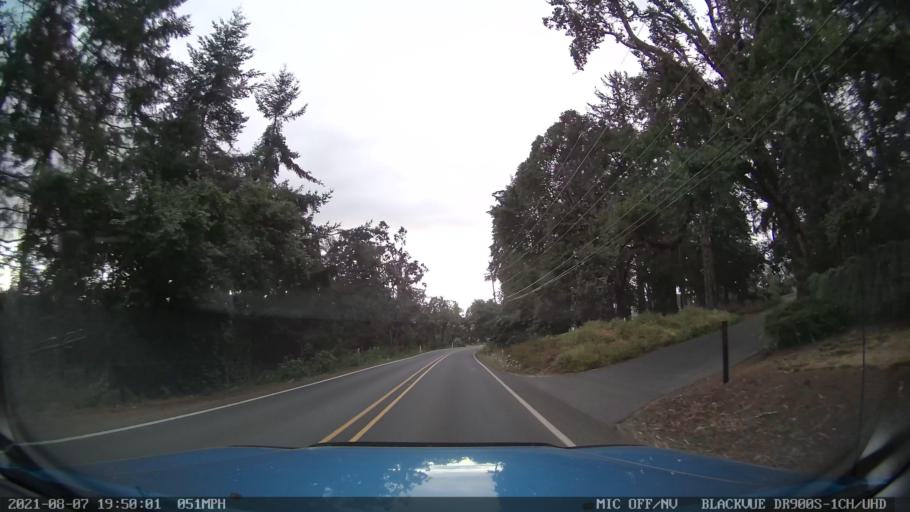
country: US
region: Oregon
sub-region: Marion County
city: Silverton
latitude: 44.9837
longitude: -122.7347
